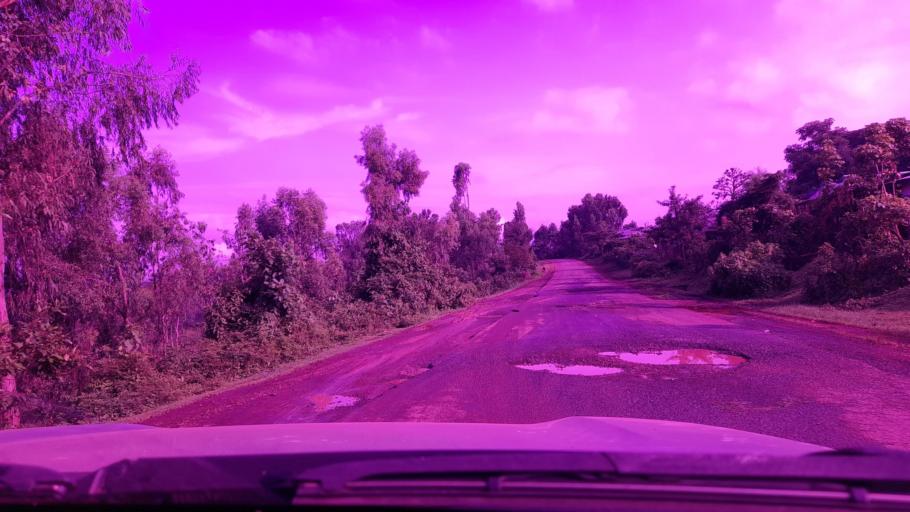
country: ET
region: Oromiya
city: Bedele
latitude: 8.1806
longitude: 36.4550
